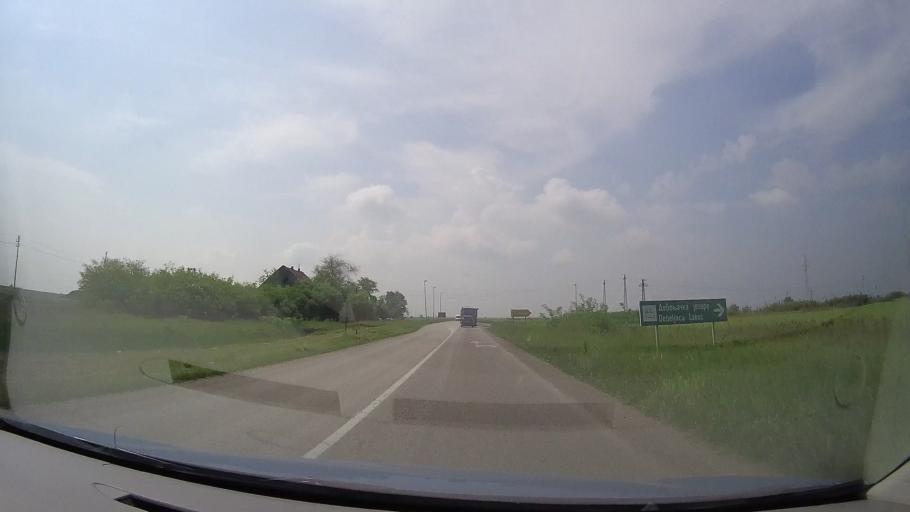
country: RS
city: Debeljaca
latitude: 45.0714
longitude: 20.6407
